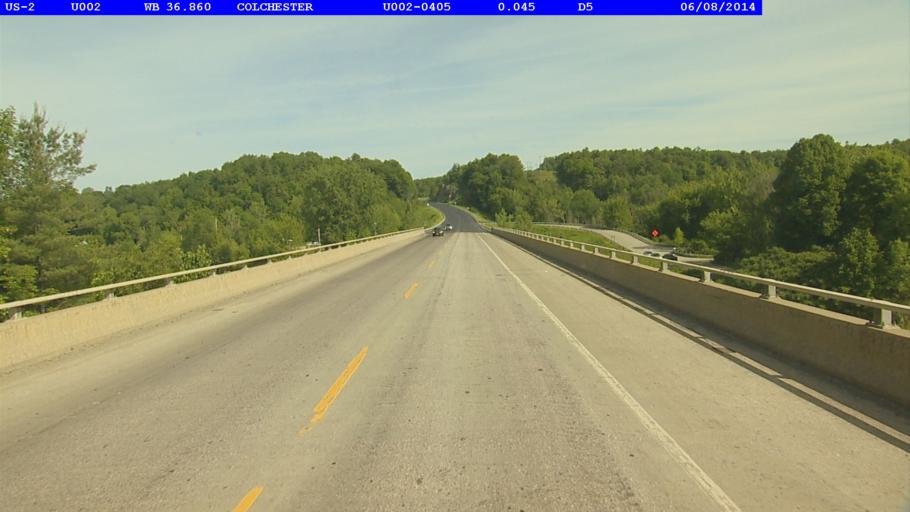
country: US
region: Vermont
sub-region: Chittenden County
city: Colchester
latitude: 44.6030
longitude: -73.2044
